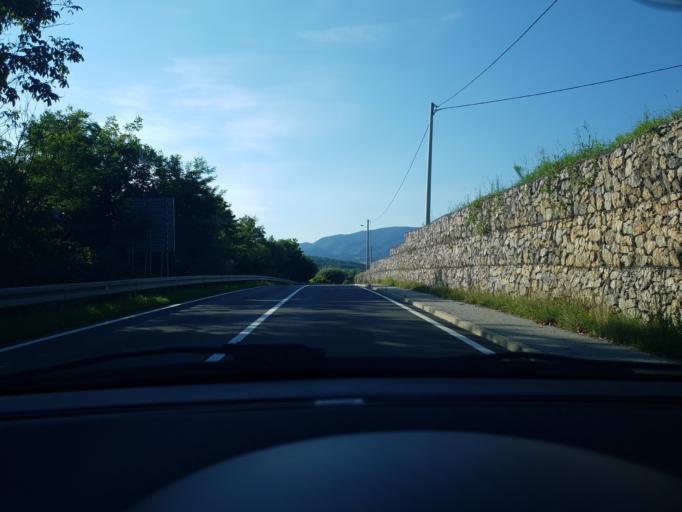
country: HR
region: Krapinsko-Zagorska
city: Mihovljan
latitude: 46.1335
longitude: 15.9383
